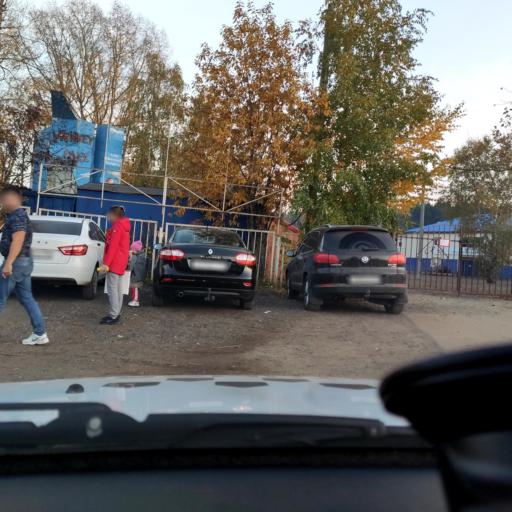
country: RU
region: Perm
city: Perm
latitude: 57.9975
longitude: 56.3203
